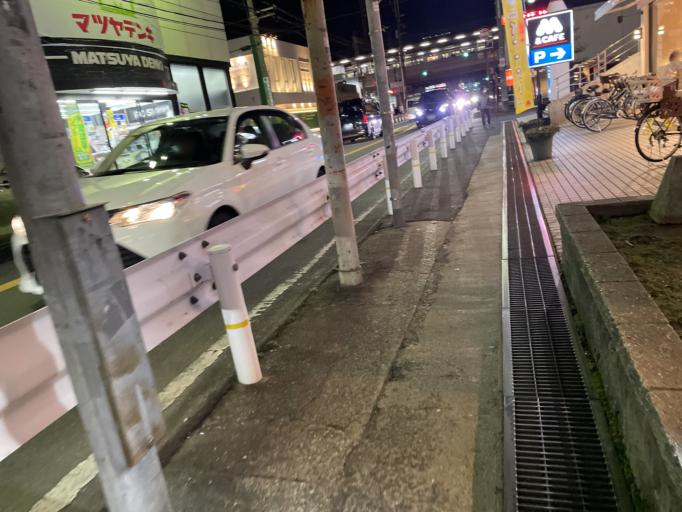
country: JP
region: Osaka
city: Yao
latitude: 34.6648
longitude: 135.5888
